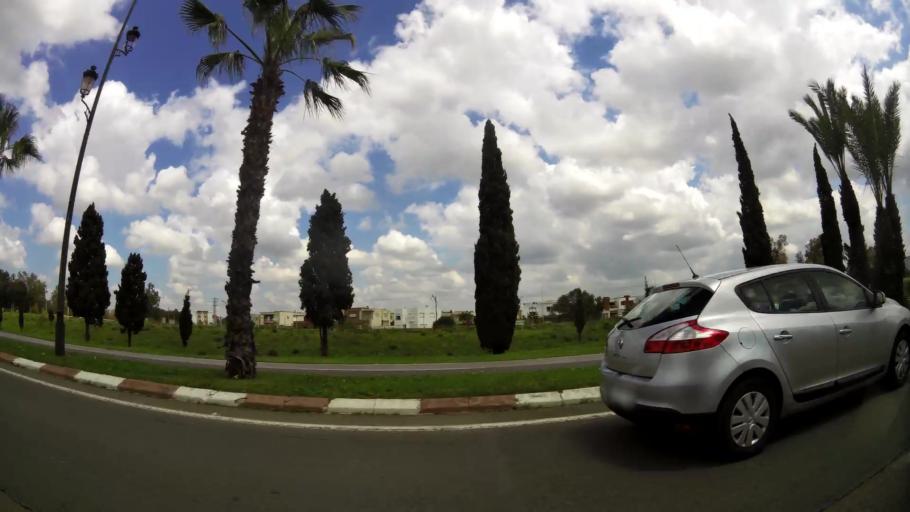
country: MA
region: Chaouia-Ouardigha
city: Nouaseur
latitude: 33.3963
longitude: -7.5686
